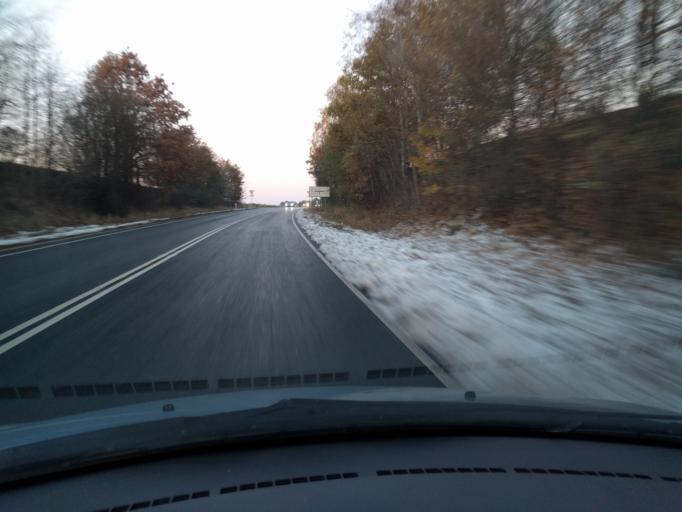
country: DK
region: South Denmark
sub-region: Nyborg Kommune
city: Nyborg
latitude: 55.3376
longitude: 10.7432
